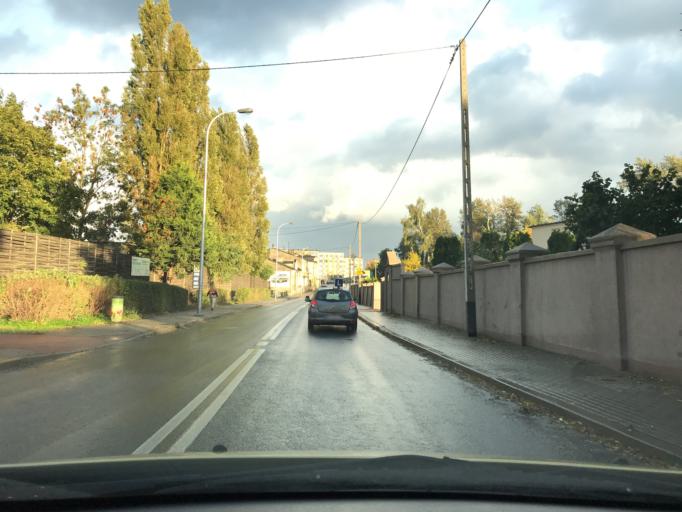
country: PL
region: Greater Poland Voivodeship
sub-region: Kalisz
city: Kalisz
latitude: 51.7612
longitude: 18.0711
